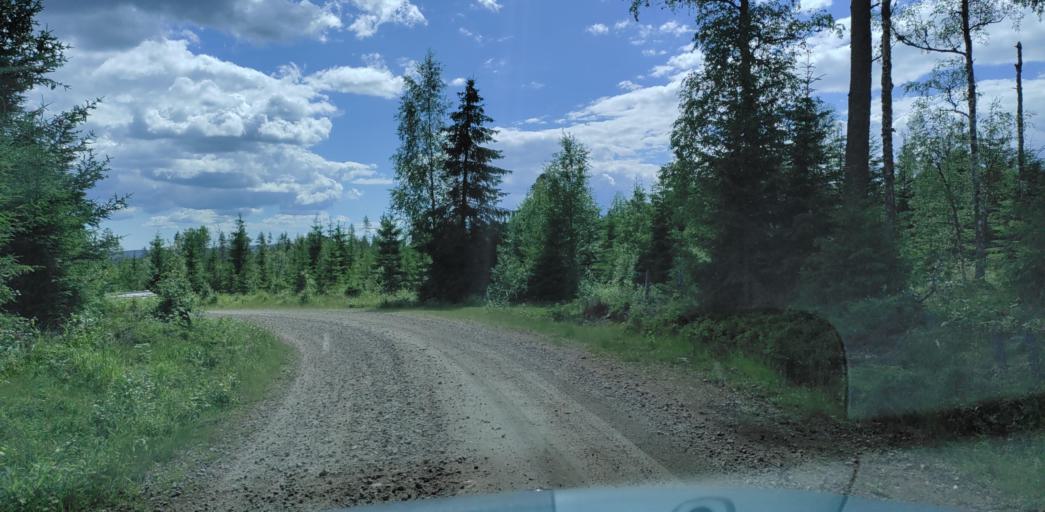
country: SE
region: Vaermland
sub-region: Hagfors Kommun
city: Ekshaerad
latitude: 60.0479
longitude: 13.3092
